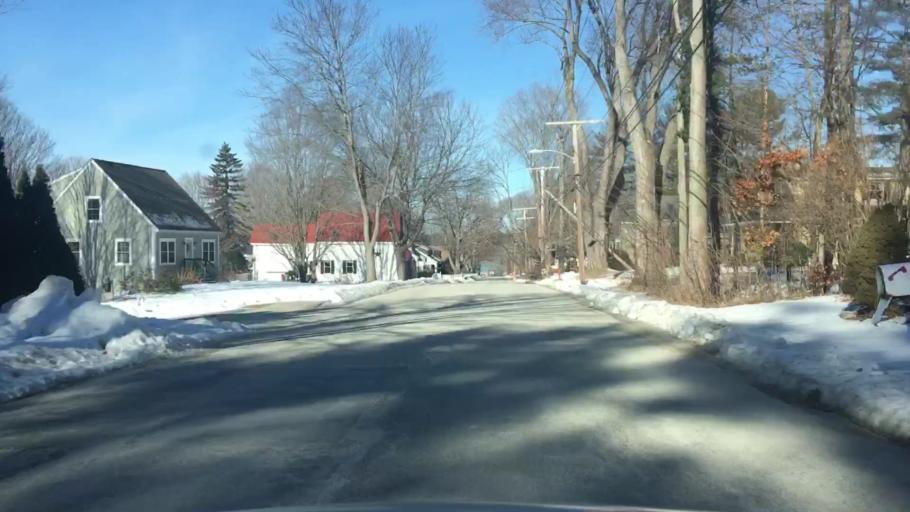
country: US
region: Maine
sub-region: Cumberland County
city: South Windham
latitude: 43.7332
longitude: -70.4197
